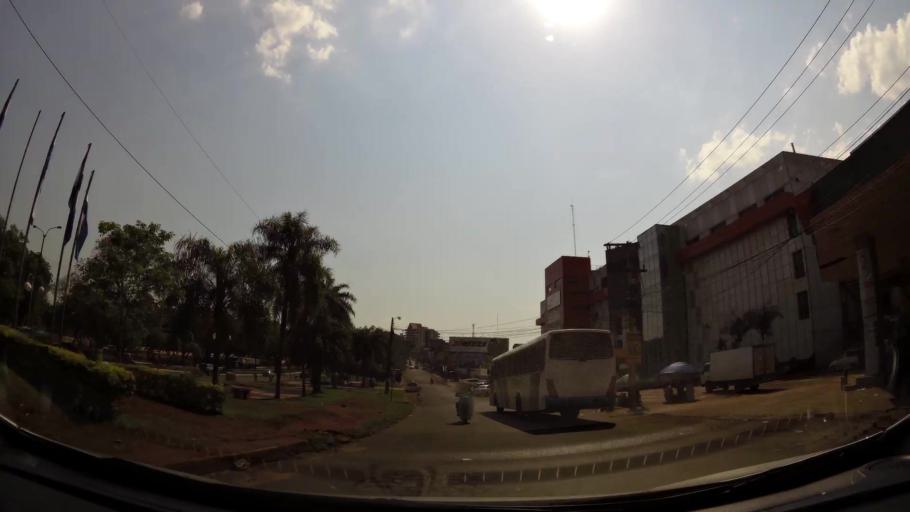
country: PY
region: Alto Parana
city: Ciudad del Este
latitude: -25.5091
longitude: -54.6167
